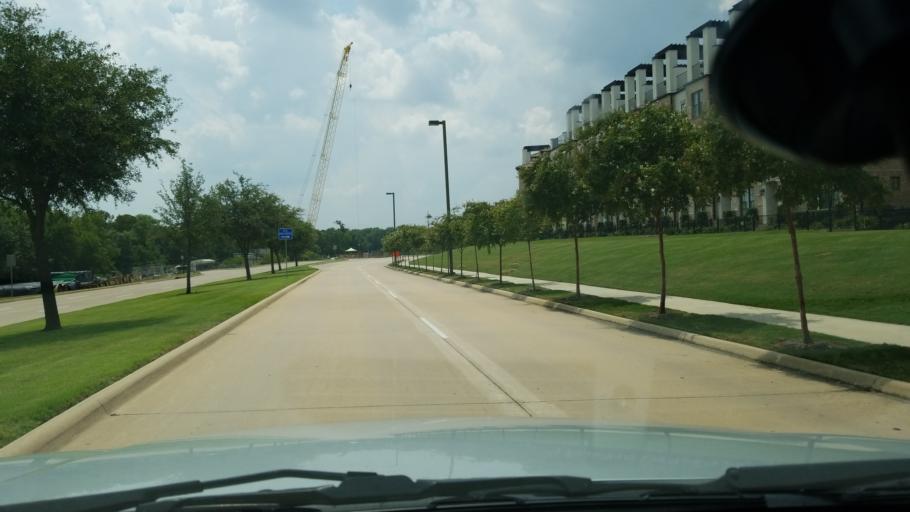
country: US
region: Texas
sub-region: Dallas County
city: Irving
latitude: 32.8635
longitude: -96.9266
